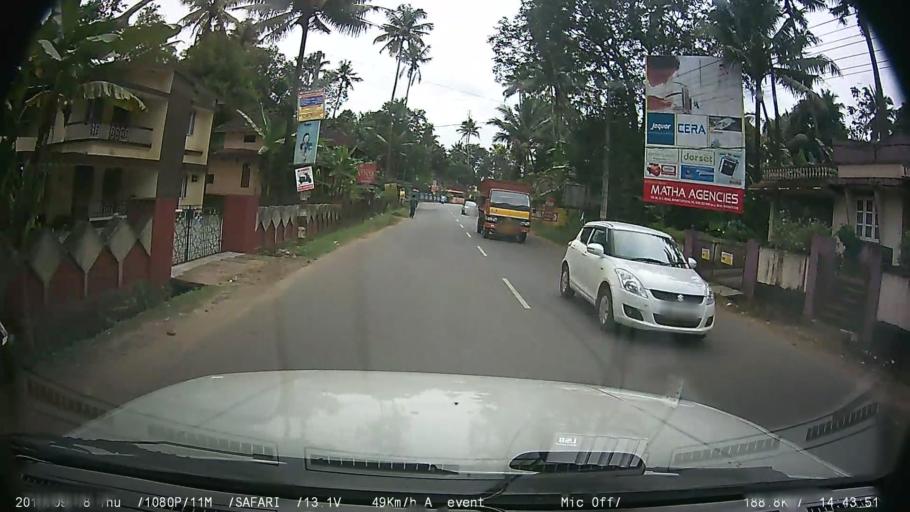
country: IN
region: Kerala
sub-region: Ernakulam
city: Muvattupula
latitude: 9.9976
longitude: 76.5994
